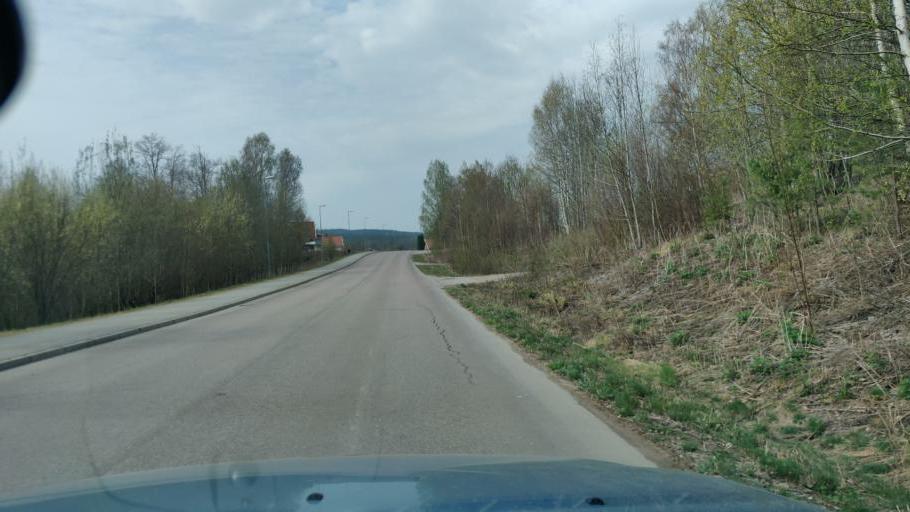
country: SE
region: Vaermland
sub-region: Munkfors Kommun
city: Munkfors
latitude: 59.8391
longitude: 13.5456
